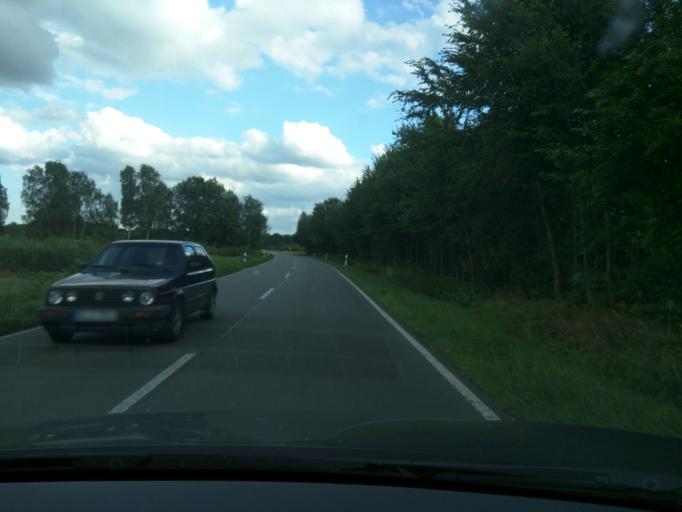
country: DE
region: Lower Saxony
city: Tespe
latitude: 53.3890
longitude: 10.4310
